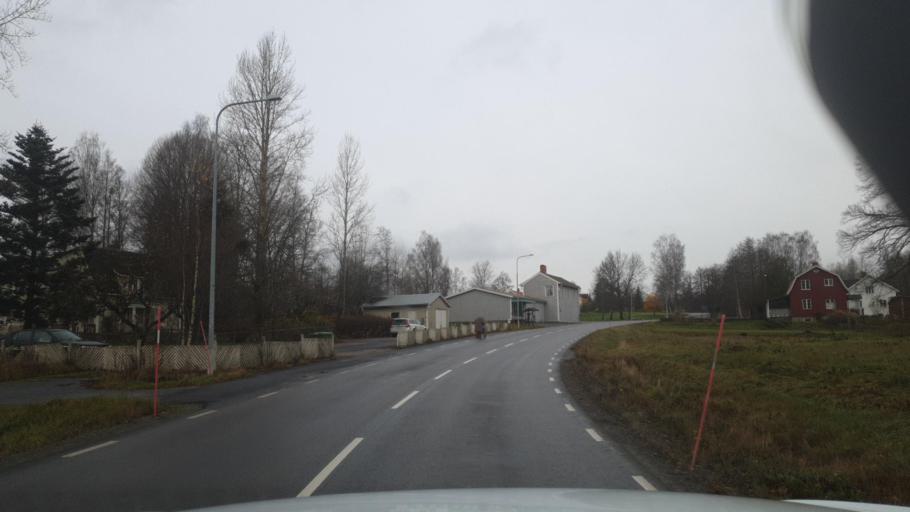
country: SE
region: Vaermland
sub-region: Arvika Kommun
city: Arvika
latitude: 59.5493
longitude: 12.5627
